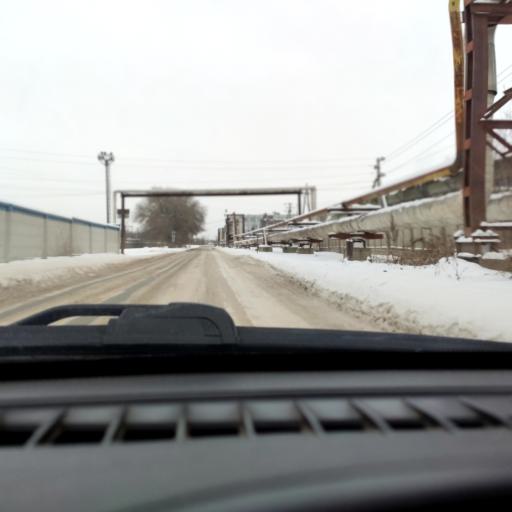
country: RU
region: Samara
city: Tol'yatti
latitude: 53.5772
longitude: 49.2779
